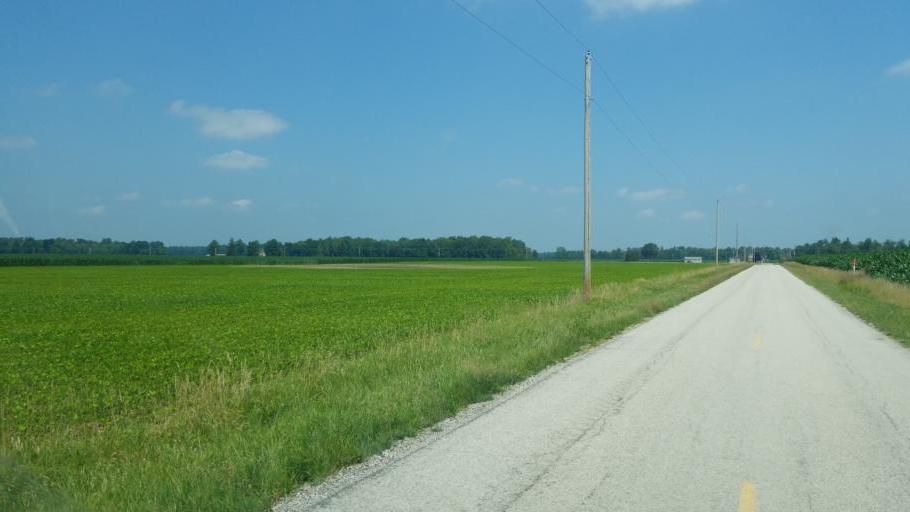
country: US
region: Ohio
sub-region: Huron County
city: Willard
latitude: 40.9891
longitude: -82.8821
